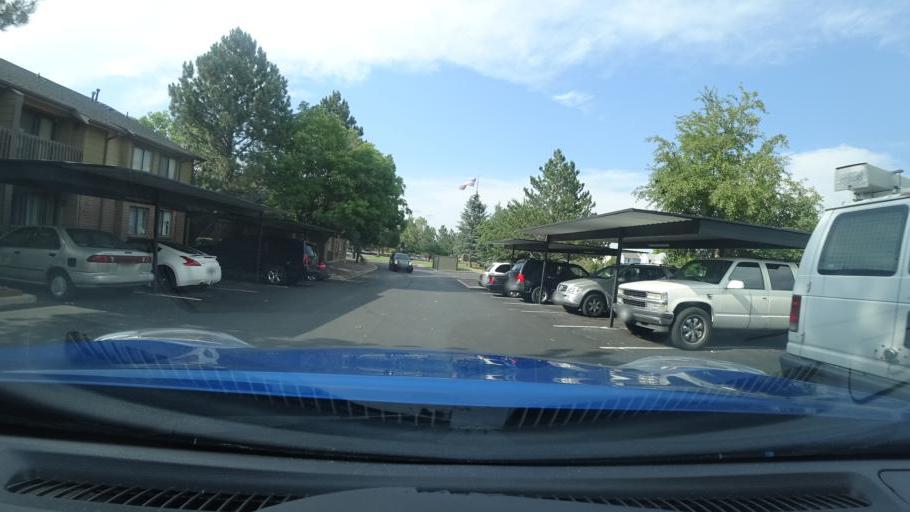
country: US
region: Colorado
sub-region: Adams County
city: Aurora
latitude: 39.6914
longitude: -104.7914
